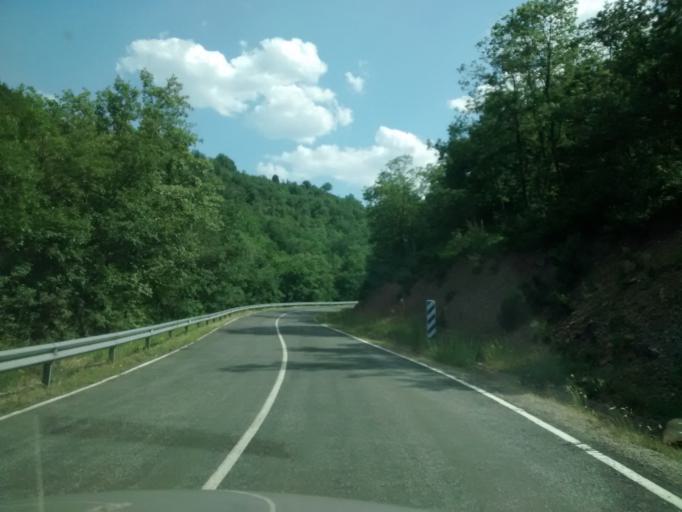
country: ES
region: La Rioja
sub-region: Provincia de La Rioja
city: Rabanera
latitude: 42.1782
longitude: -2.4845
